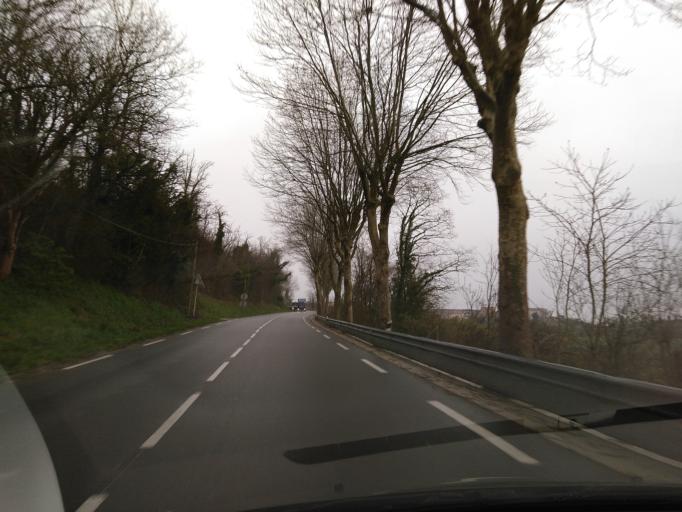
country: FR
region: Aquitaine
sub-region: Departement du Lot-et-Garonne
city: Saint-Hilaire
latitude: 44.4918
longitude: 0.6703
